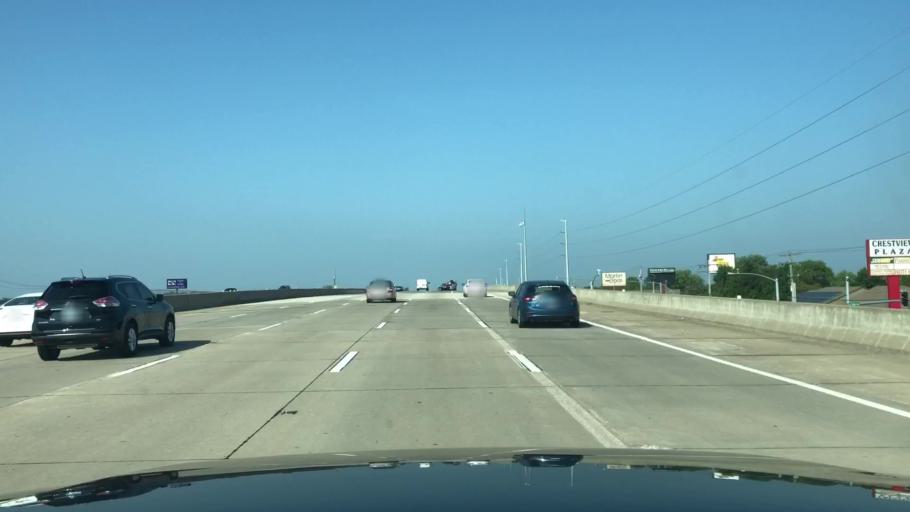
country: US
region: Missouri
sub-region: Saint Charles County
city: Saint Peters
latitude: 38.7514
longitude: -90.5621
